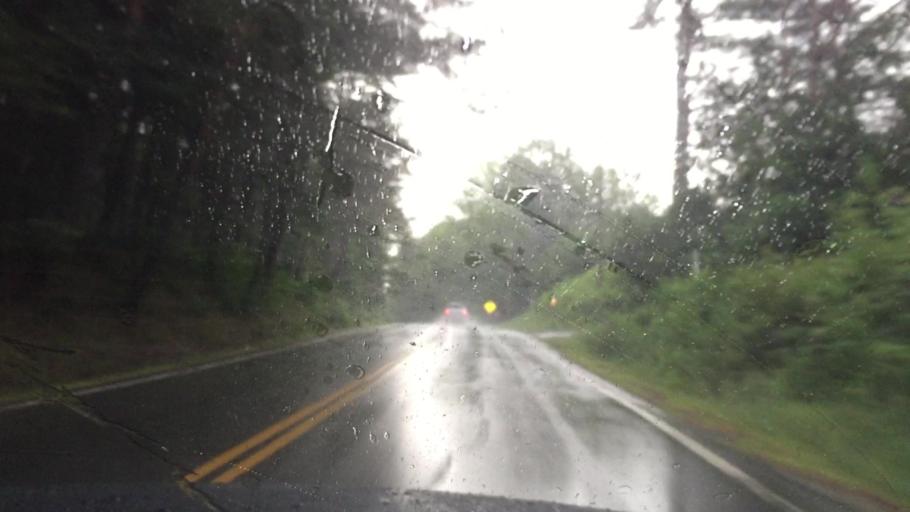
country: US
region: New Hampshire
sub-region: Grafton County
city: Holderness
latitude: 43.7189
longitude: -71.5378
